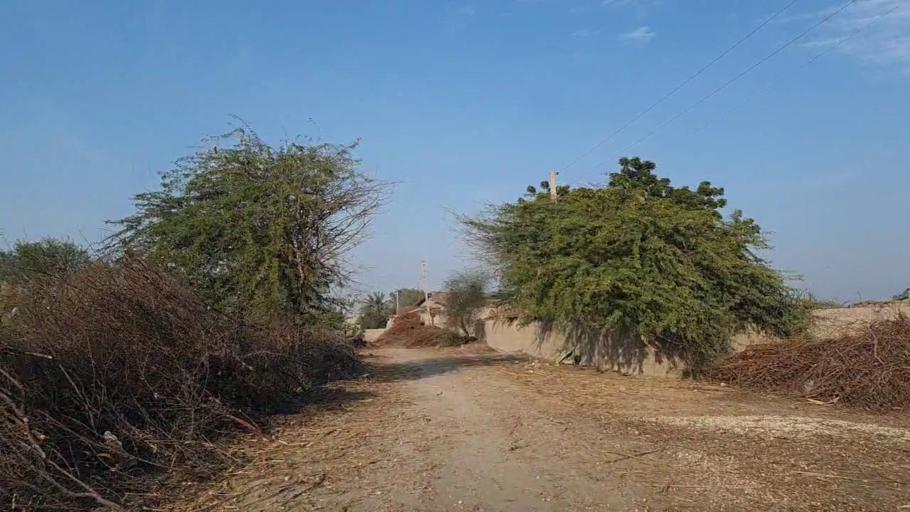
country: PK
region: Sindh
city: Nawabshah
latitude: 26.3733
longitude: 68.4949
